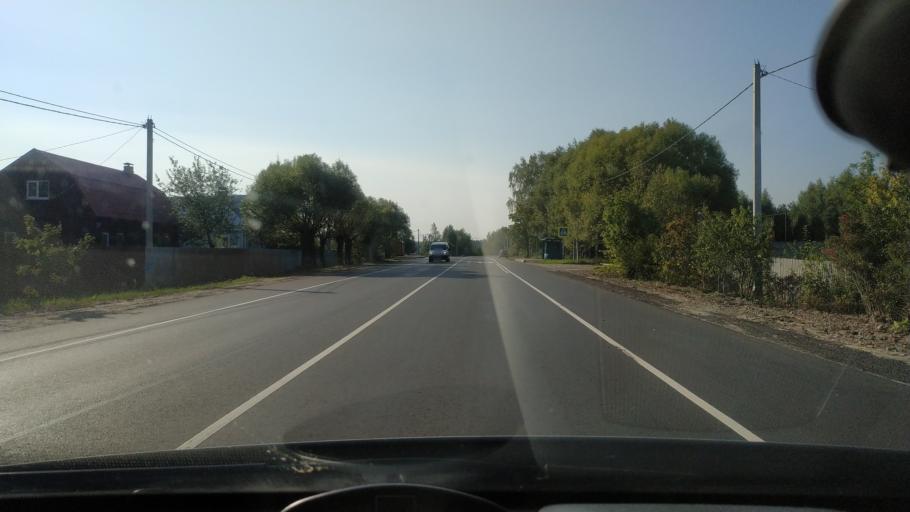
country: RU
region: Moskovskaya
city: Misheronskiy
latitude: 55.6501
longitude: 39.7556
